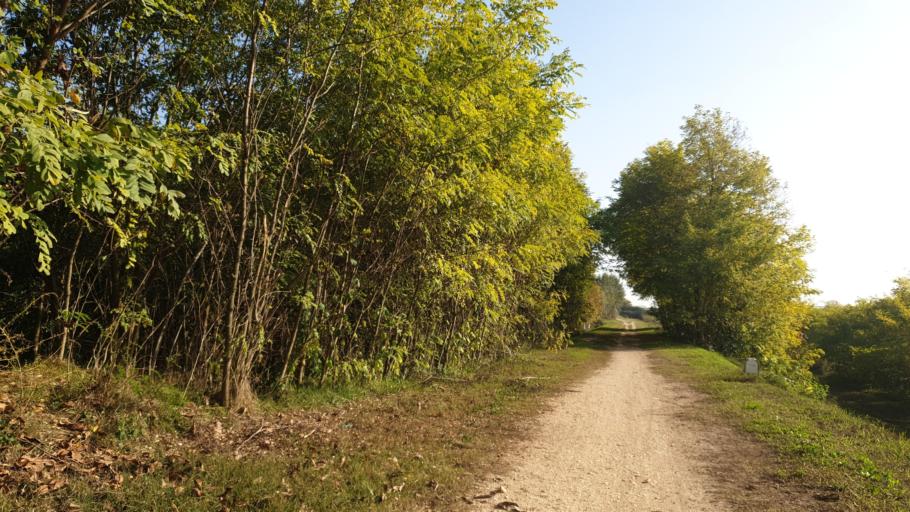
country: IT
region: Veneto
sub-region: Provincia di Venezia
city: Vigonovo
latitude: 45.3944
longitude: 12.0103
